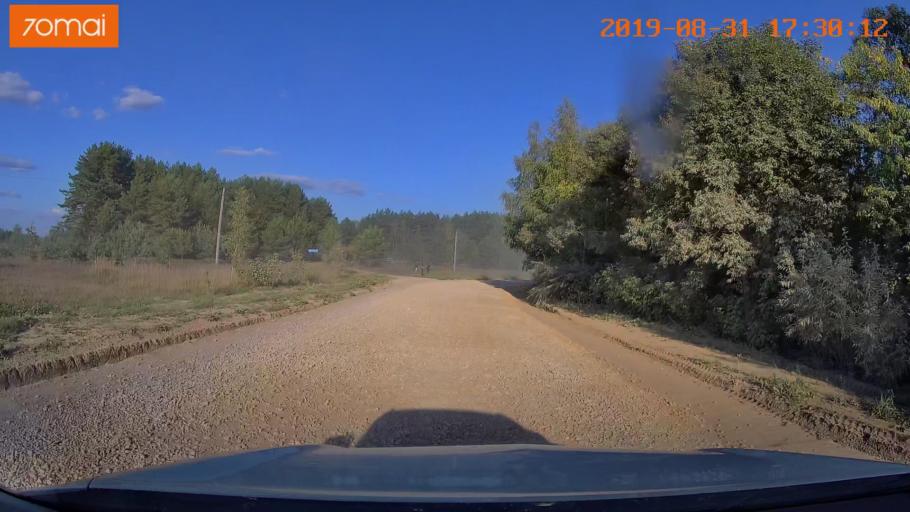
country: RU
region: Kaluga
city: Detchino
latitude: 54.8110
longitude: 36.3323
